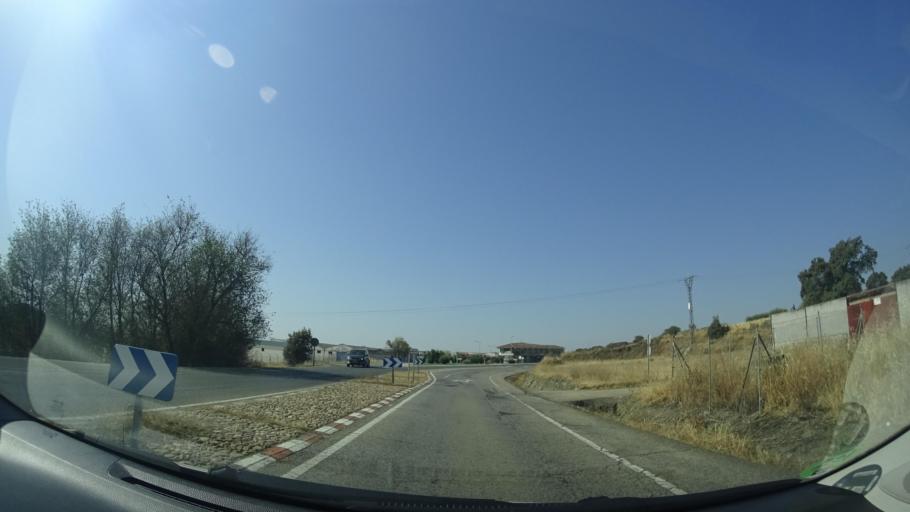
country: ES
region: Extremadura
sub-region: Provincia de Caceres
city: Miajadas
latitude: 39.1610
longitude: -5.8988
